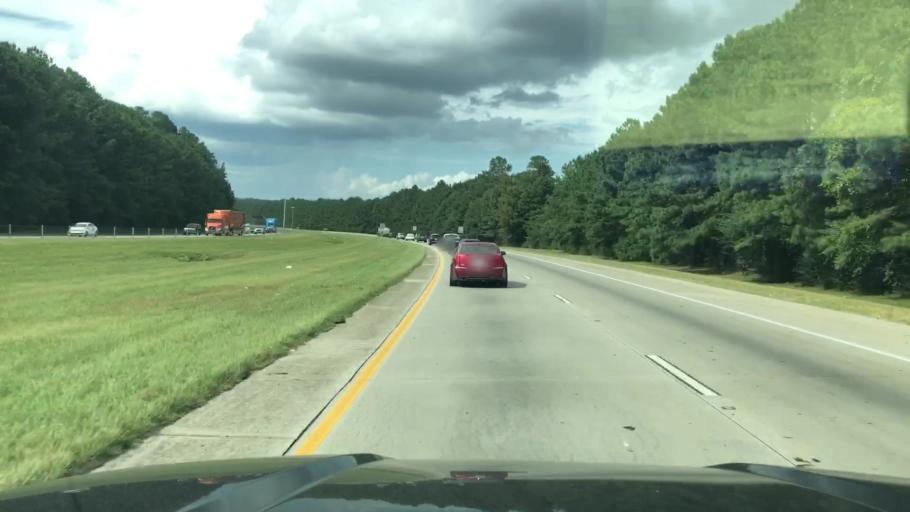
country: US
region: Georgia
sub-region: Clayton County
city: Lake City
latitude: 33.5917
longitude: -84.2824
